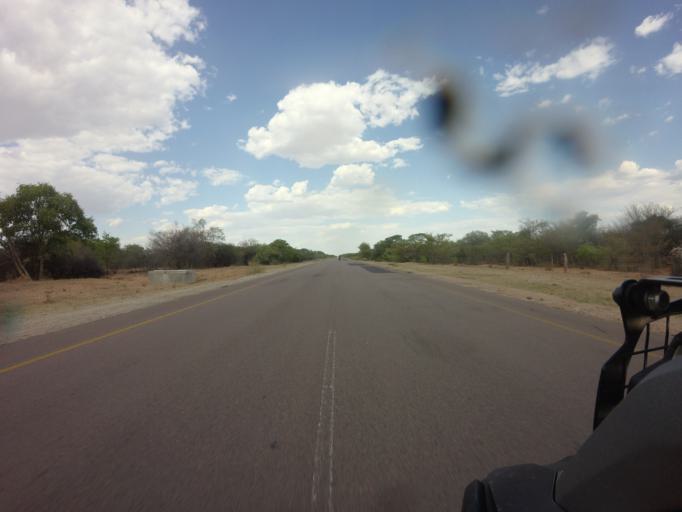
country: AO
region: Cunene
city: Ondjiva
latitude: -16.7345
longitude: 15.1522
